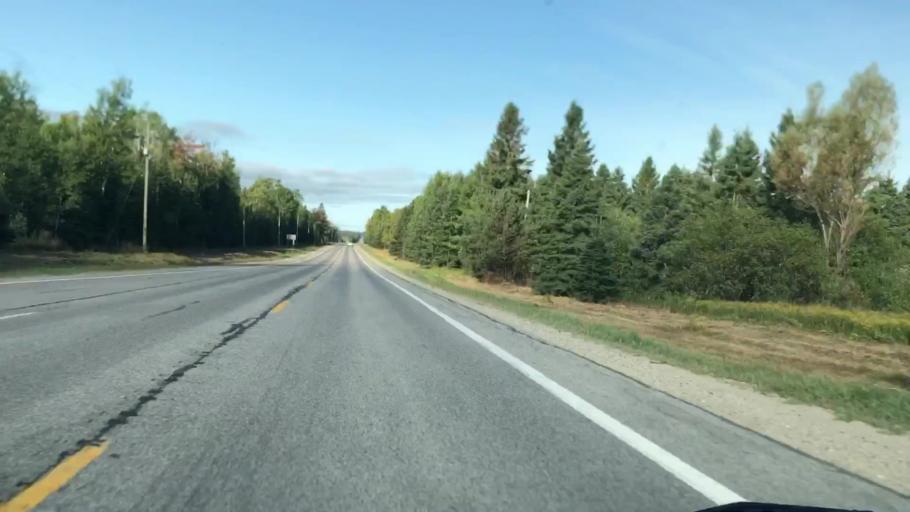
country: US
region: Michigan
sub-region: Luce County
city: Newberry
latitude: 46.3034
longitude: -85.3643
